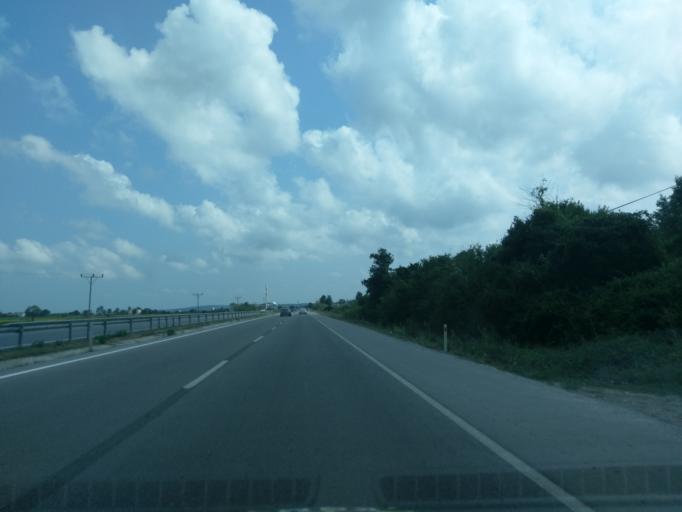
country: TR
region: Samsun
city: Bafra
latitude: 41.6020
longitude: 35.7548
